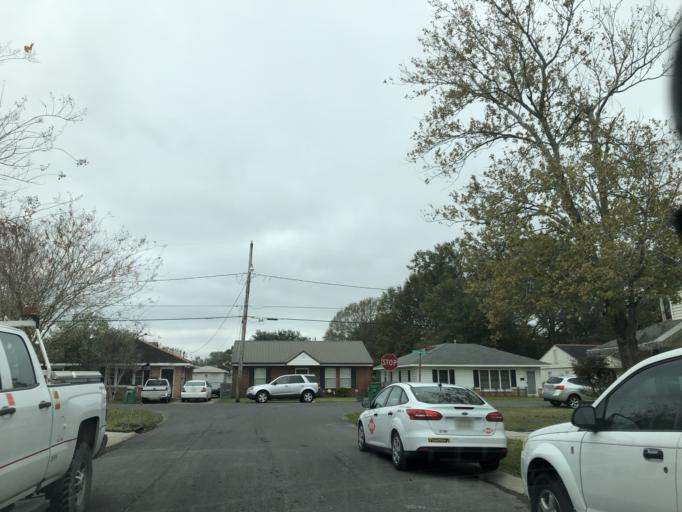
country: US
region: Louisiana
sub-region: Jefferson Parish
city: Metairie Terrace
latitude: 29.9792
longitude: -90.1627
